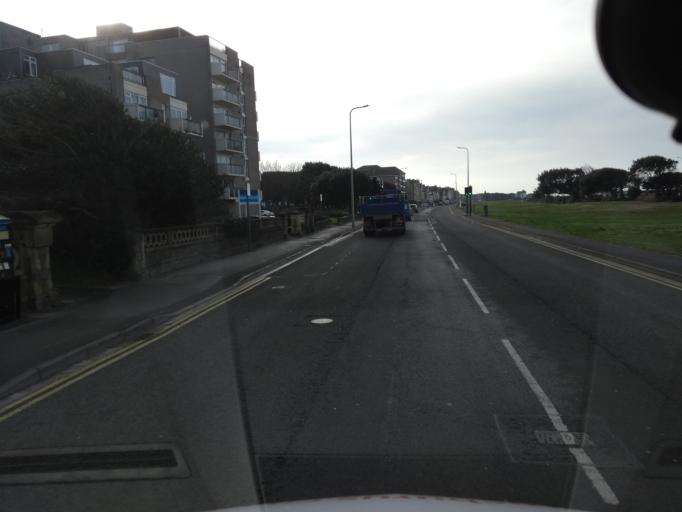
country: GB
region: England
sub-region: North Somerset
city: Weston-super-Mare
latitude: 51.3436
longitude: -2.9806
